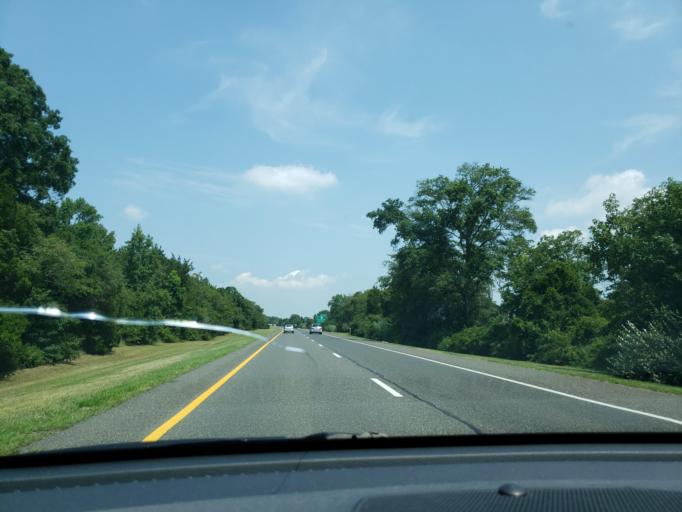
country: US
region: New Jersey
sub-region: Cape May County
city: Erma
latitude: 38.9791
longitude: -74.8888
